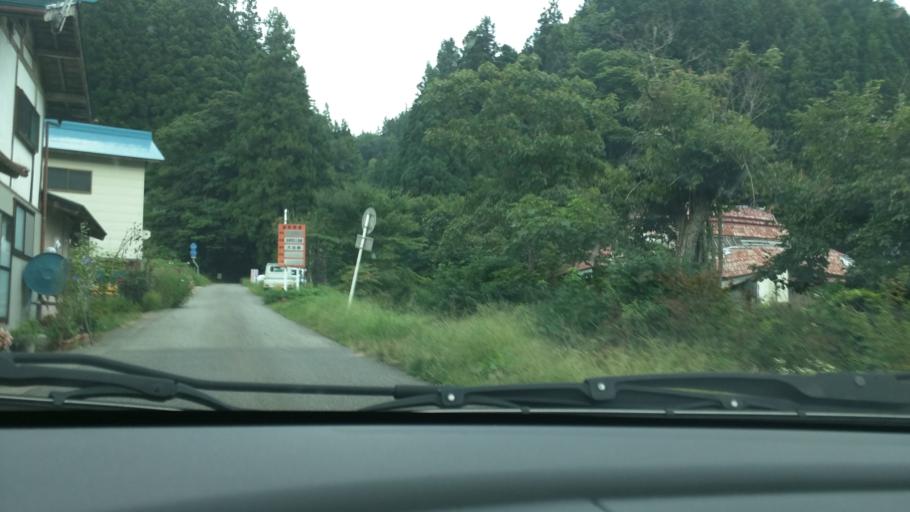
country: JP
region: Fukushima
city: Kitakata
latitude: 37.4469
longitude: 139.6515
